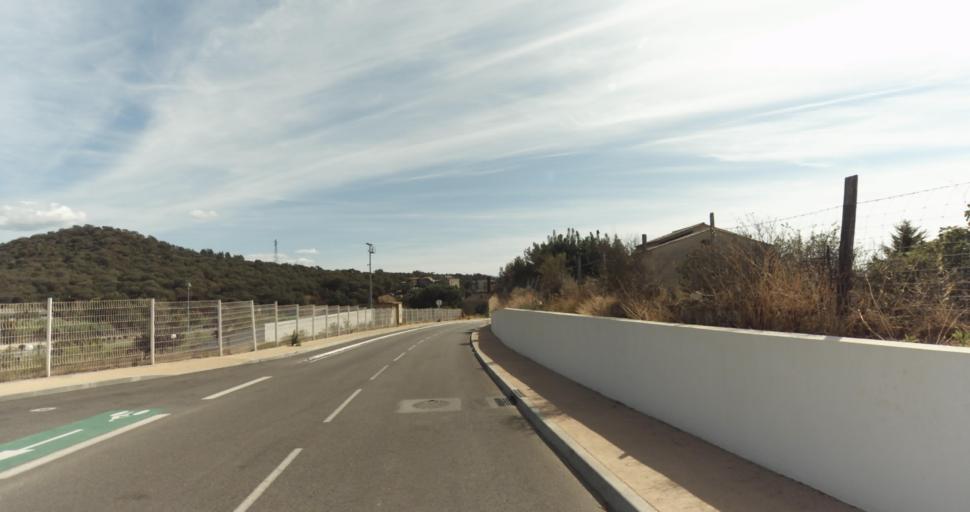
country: FR
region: Corsica
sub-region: Departement de la Corse-du-Sud
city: Ajaccio
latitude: 41.9473
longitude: 8.7579
